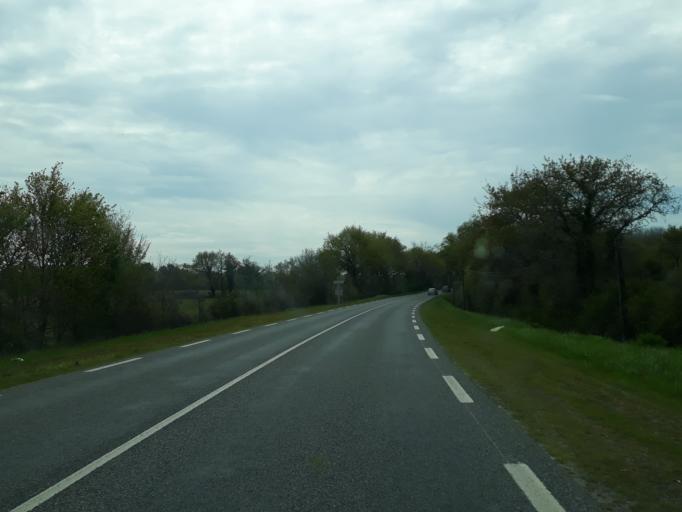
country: FR
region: Pays de la Loire
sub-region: Departement de la Loire-Atlantique
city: Saint-Molf
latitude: 47.3612
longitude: -2.4131
